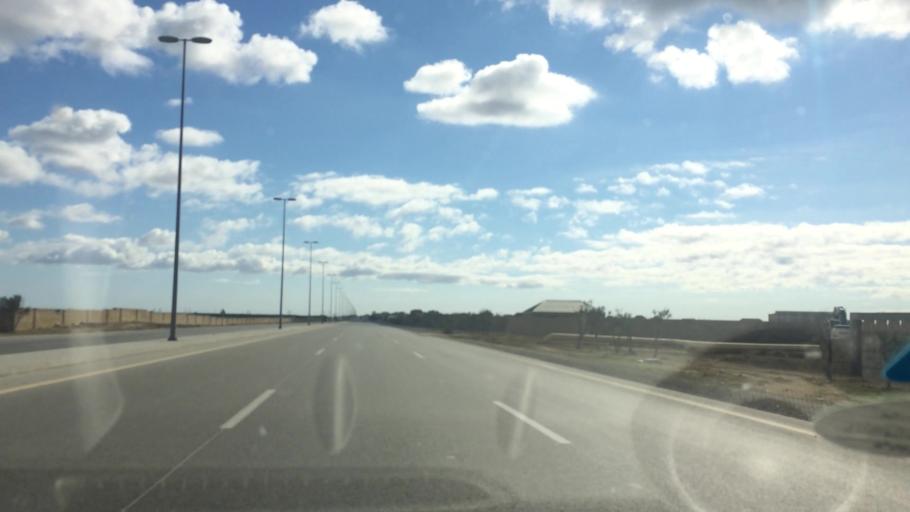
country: AZ
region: Baki
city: Qala
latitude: 40.4553
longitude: 50.1456
